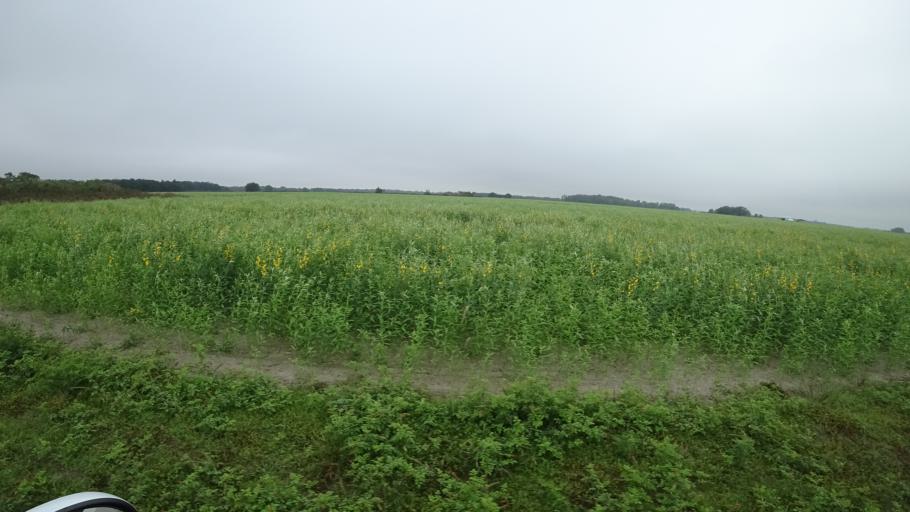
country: US
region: Florida
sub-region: Sarasota County
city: Warm Mineral Springs
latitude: 27.2953
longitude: -82.1584
